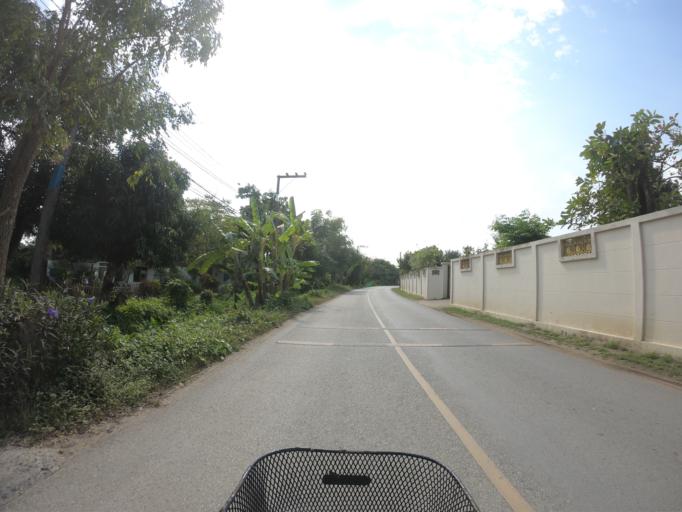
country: TH
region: Chiang Mai
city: Saraphi
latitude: 18.7068
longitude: 99.0612
